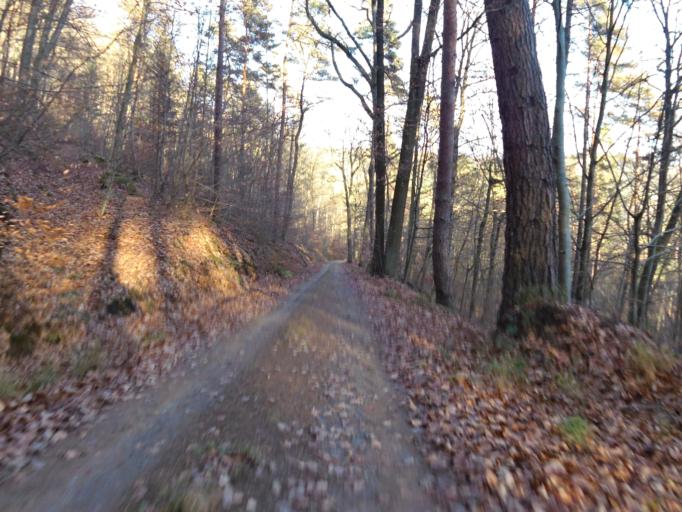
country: DE
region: Rheinland-Pfalz
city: Altleiningen
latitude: 49.4814
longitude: 8.0933
